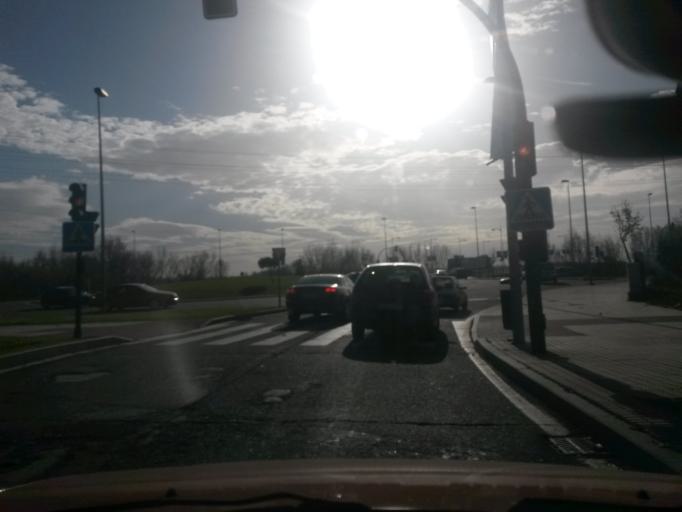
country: ES
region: Castille and Leon
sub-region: Provincia de Salamanca
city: Salamanca
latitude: 40.9618
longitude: -5.6451
